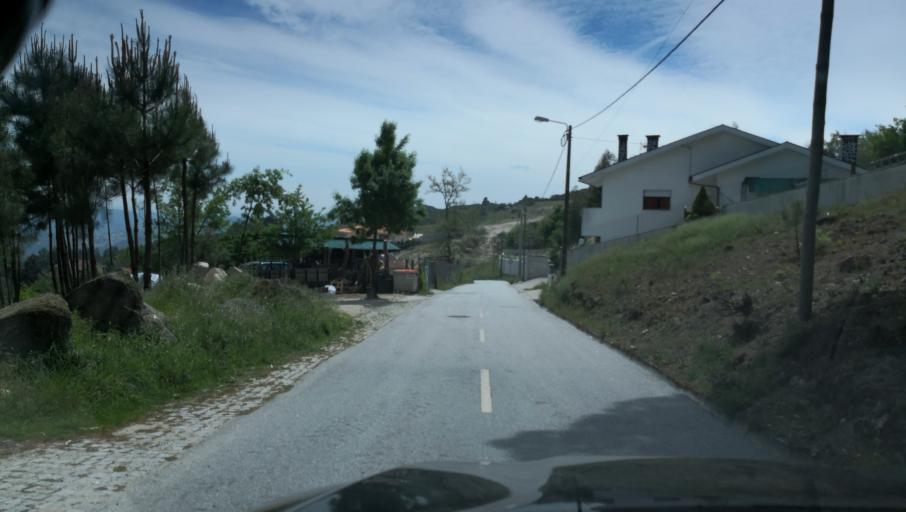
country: PT
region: Vila Real
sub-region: Vila Real
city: Vila Real
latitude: 41.3148
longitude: -7.7865
